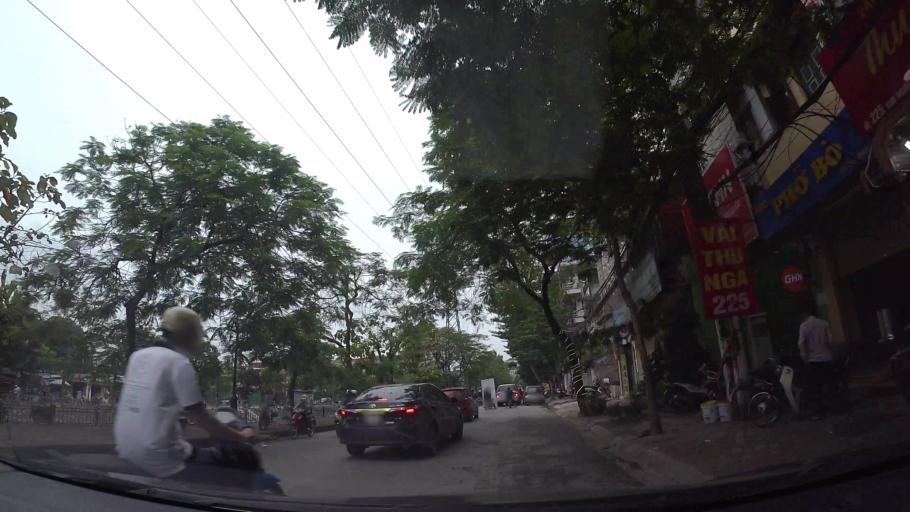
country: VN
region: Ha Noi
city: Hai BaTrung
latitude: 21.0050
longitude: 105.8616
